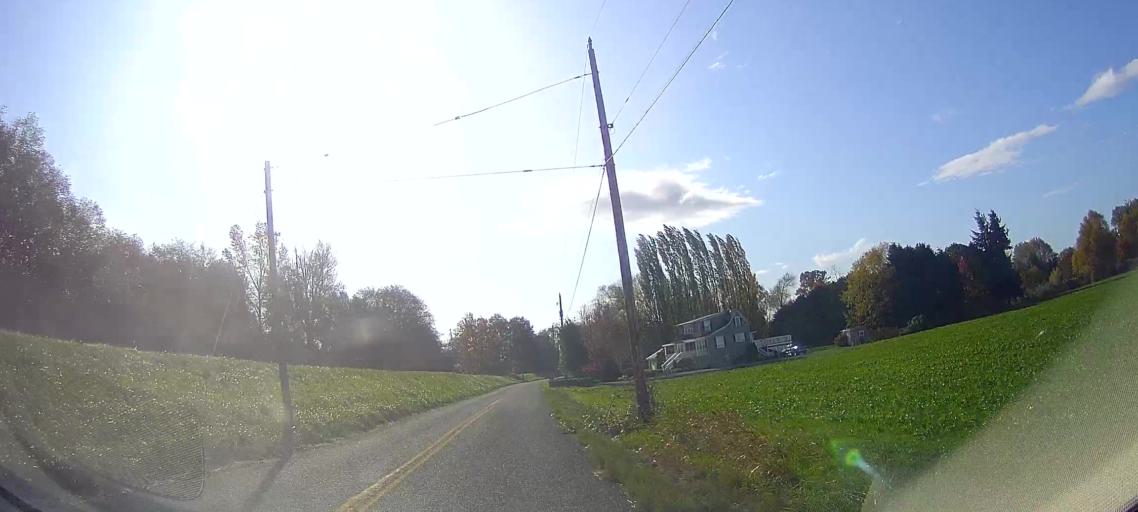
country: US
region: Washington
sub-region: Snohomish County
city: Stanwood
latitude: 48.3301
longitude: -122.3531
